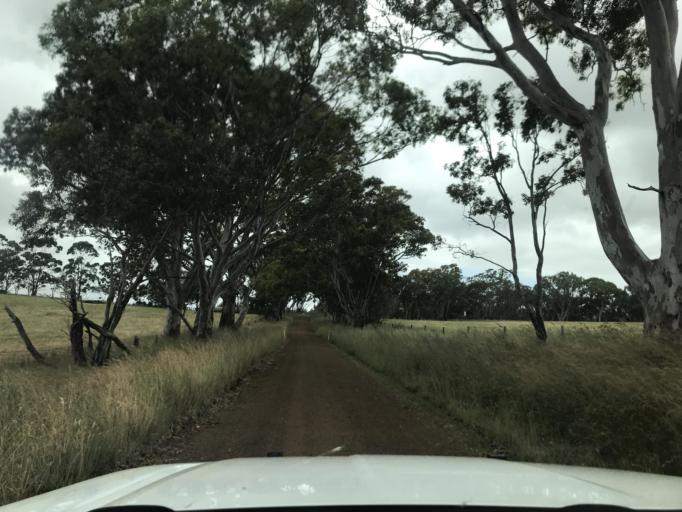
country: AU
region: South Australia
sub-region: Wattle Range
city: Penola
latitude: -37.2345
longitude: 141.4763
